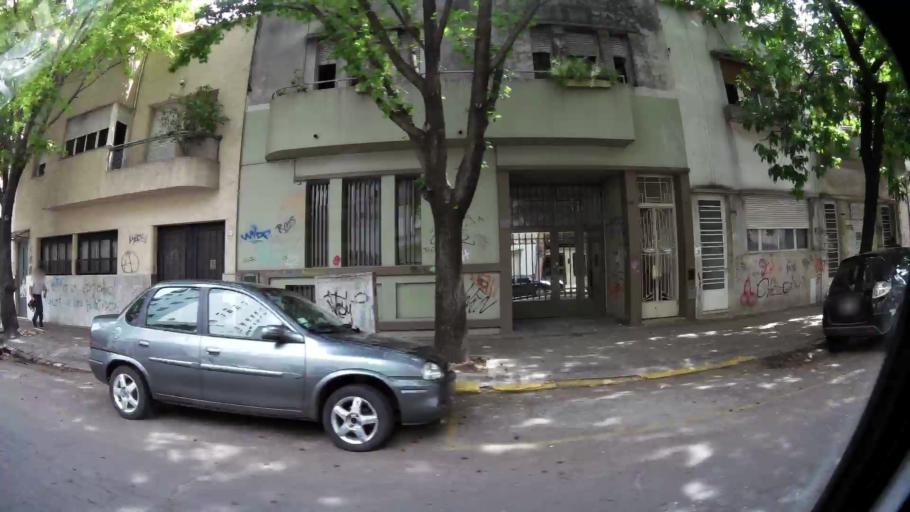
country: AR
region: Buenos Aires
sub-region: Partido de La Plata
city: La Plata
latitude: -34.9196
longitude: -57.9481
